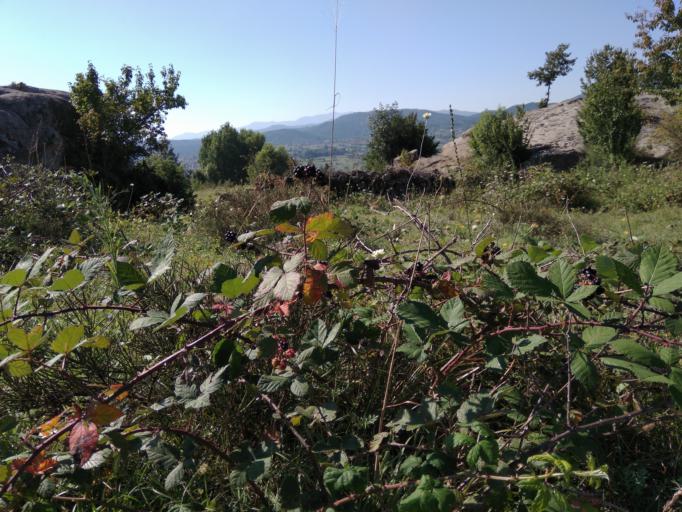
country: BG
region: Smolyan
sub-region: Obshtina Zlatograd
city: Zlatograd
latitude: 41.3824
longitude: 25.2229
